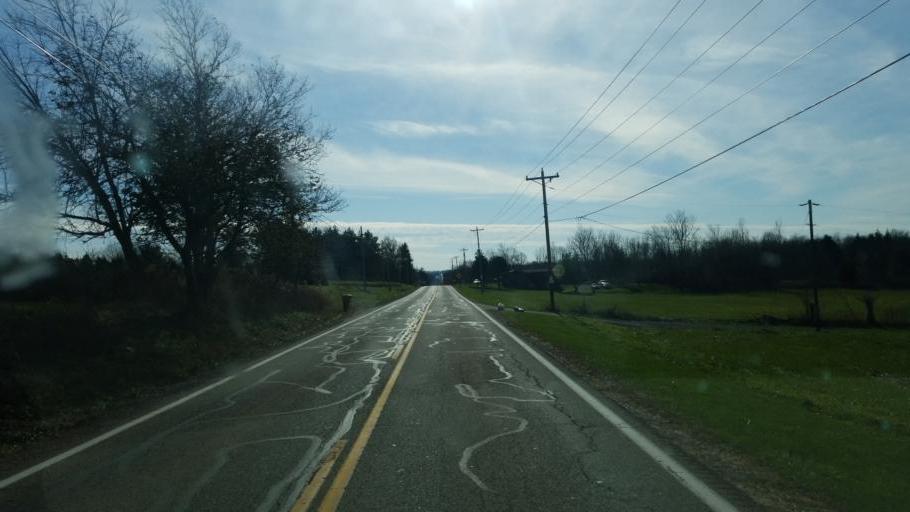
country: US
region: Ohio
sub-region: Richland County
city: Lexington
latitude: 40.6548
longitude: -82.6637
